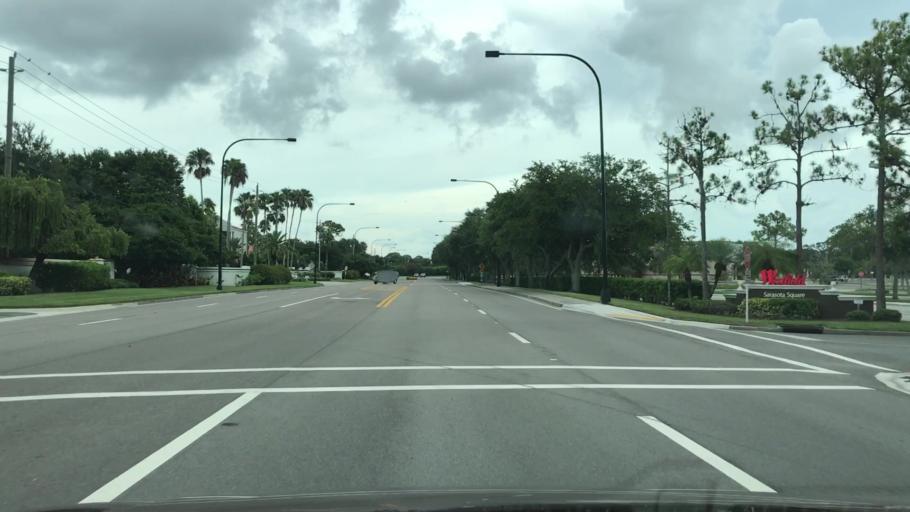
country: US
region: Florida
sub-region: Sarasota County
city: Vamo
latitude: 27.2367
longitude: -82.4925
